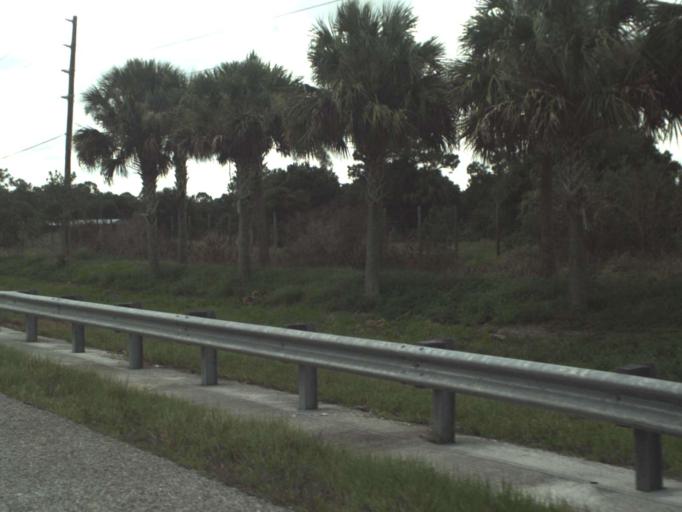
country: US
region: Florida
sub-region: Indian River County
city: Fellsmere
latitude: 27.6596
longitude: -80.7921
